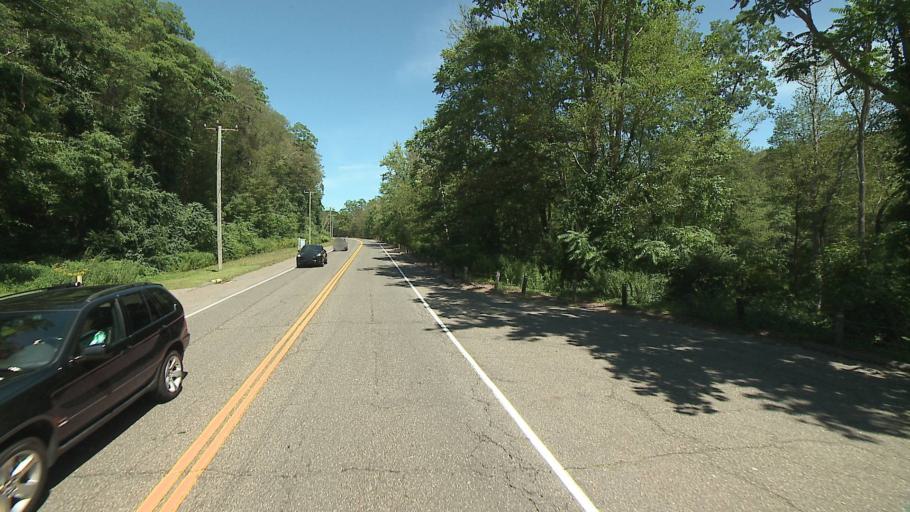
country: US
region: Connecticut
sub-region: Hartford County
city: Collinsville
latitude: 41.7949
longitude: -72.9255
